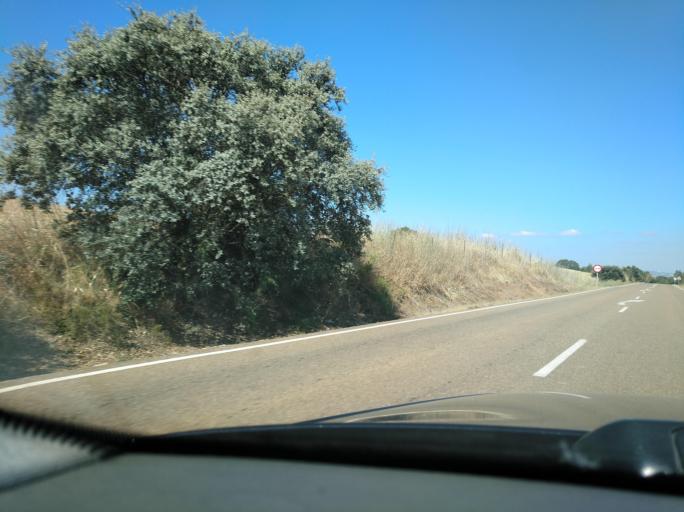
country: ES
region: Extremadura
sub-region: Provincia de Badajoz
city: Olivenza
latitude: 38.6989
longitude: -7.1457
